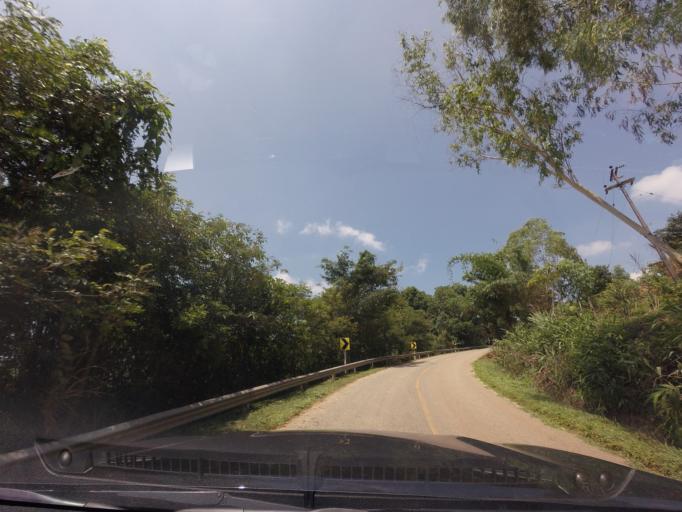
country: TH
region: Loei
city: Na Haeo
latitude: 17.5945
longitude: 100.9045
